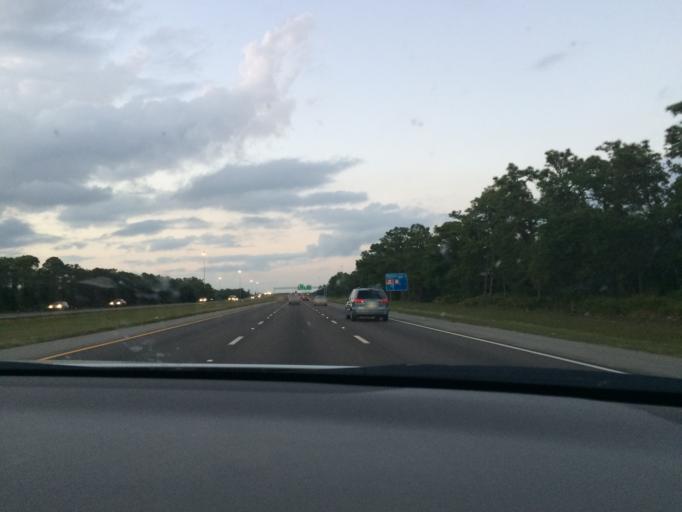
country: US
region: Florida
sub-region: Sarasota County
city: Desoto Lakes
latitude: 27.4320
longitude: -82.4594
